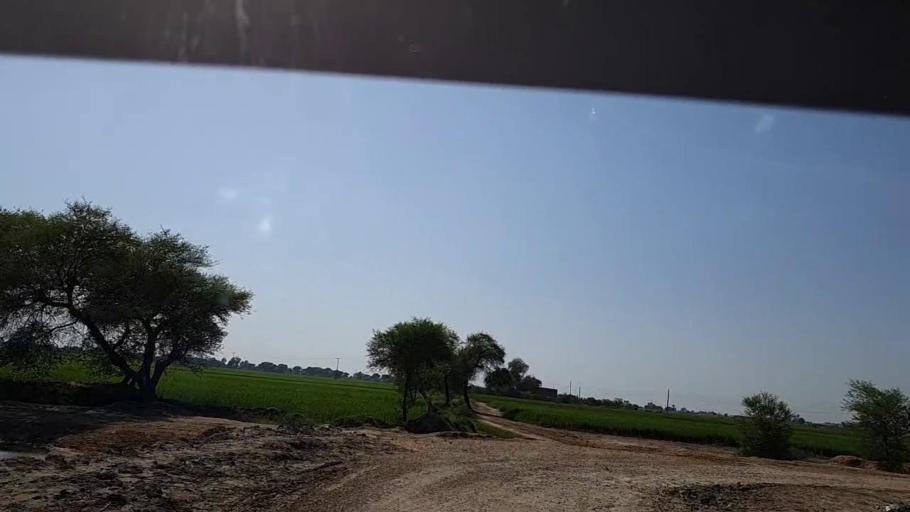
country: PK
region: Sindh
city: Tangwani
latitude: 28.3308
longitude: 69.0725
